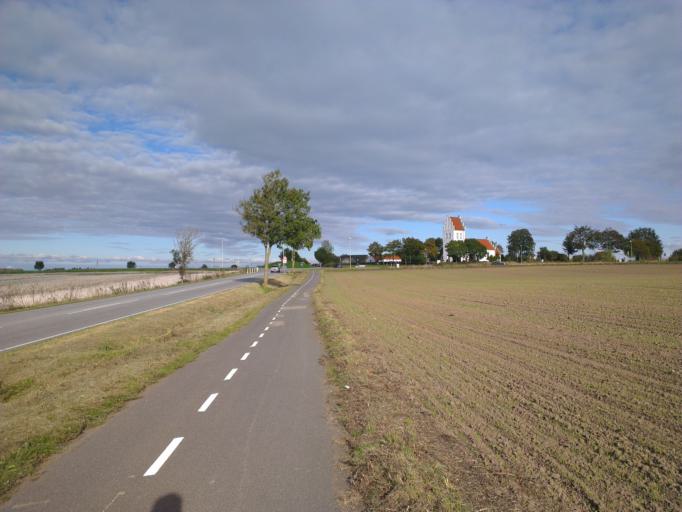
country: DK
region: Zealand
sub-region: Lejre Kommune
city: Ejby
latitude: 55.7024
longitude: 11.8850
